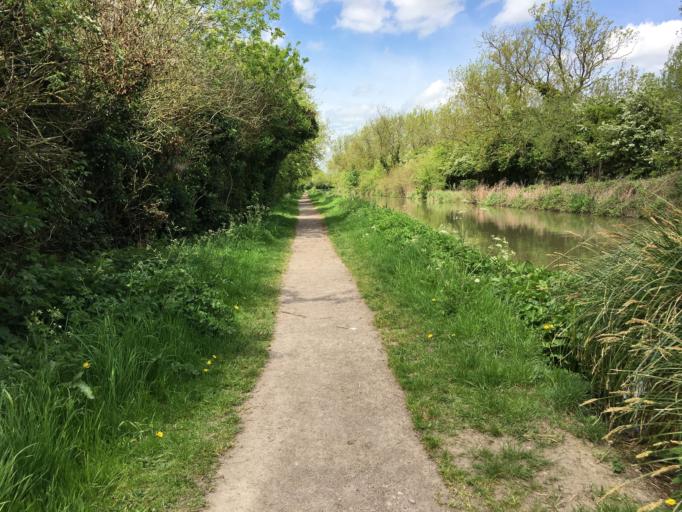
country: GB
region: England
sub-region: Warwickshire
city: Rugby
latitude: 52.3809
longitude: -1.2382
